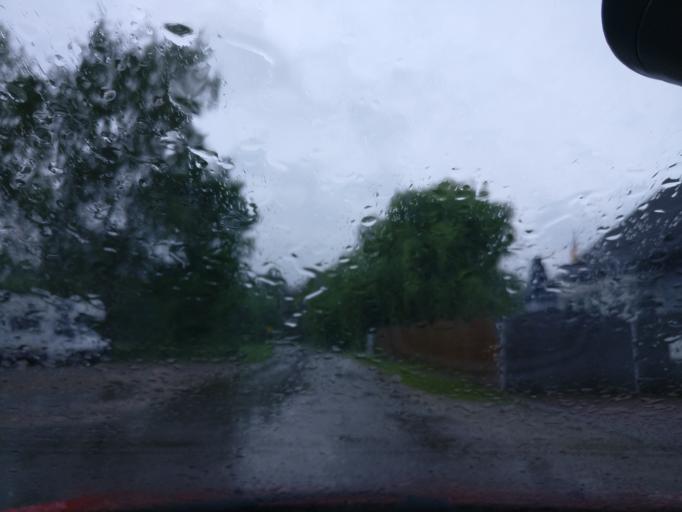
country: DE
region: Bavaria
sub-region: Upper Bavaria
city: Karlsfeld
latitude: 48.2437
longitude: 11.4596
